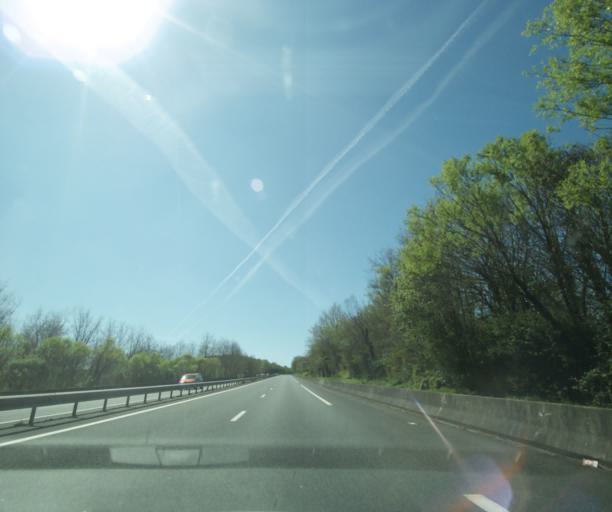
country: FR
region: Limousin
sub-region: Departement de la Haute-Vienne
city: Saint-Sulpice-les-Feuilles
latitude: 46.3789
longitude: 1.4469
